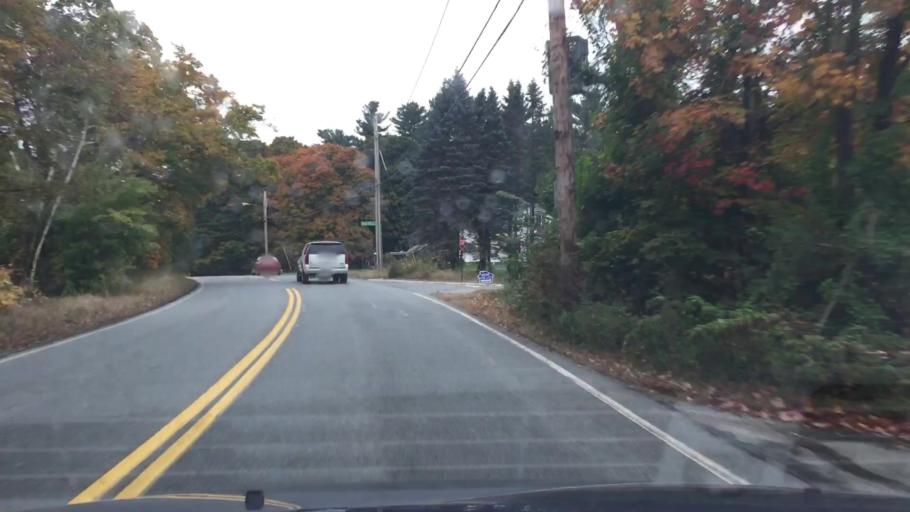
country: US
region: Massachusetts
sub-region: Middlesex County
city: Tyngsboro
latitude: 42.6970
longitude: -71.3876
